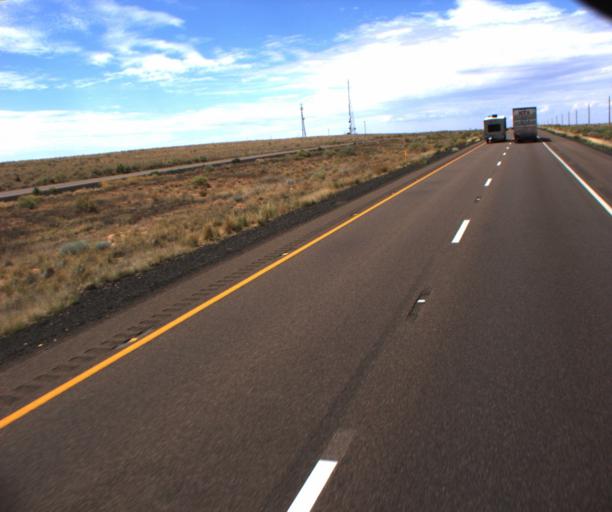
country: US
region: Arizona
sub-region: Navajo County
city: Holbrook
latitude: 35.0275
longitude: -109.8390
